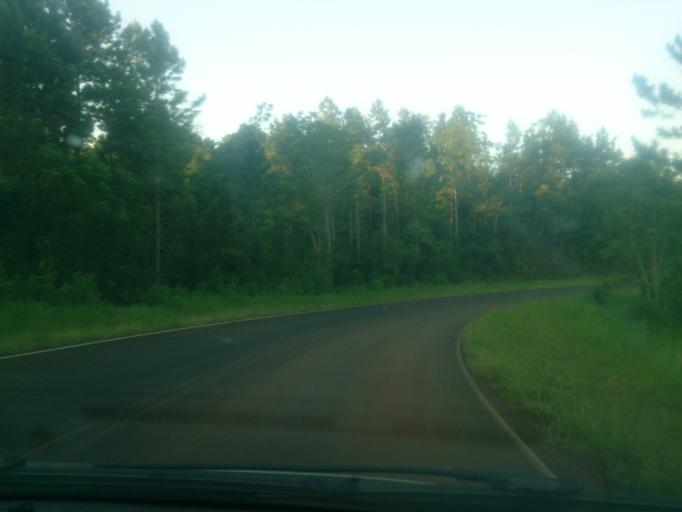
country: AR
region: Misiones
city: Panambi
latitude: -27.6650
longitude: -54.9150
